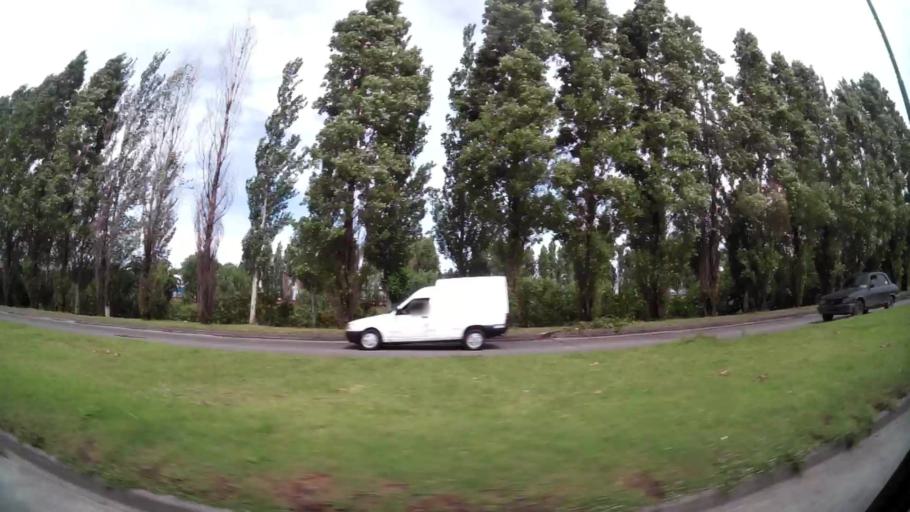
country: AR
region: Buenos Aires F.D.
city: Villa Lugano
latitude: -34.6653
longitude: -58.4281
